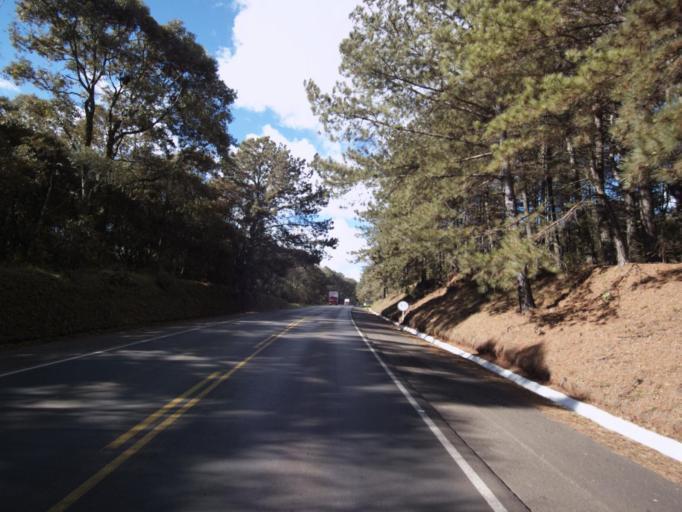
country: BR
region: Santa Catarina
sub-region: Joacaba
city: Joacaba
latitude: -26.9745
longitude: -51.7673
